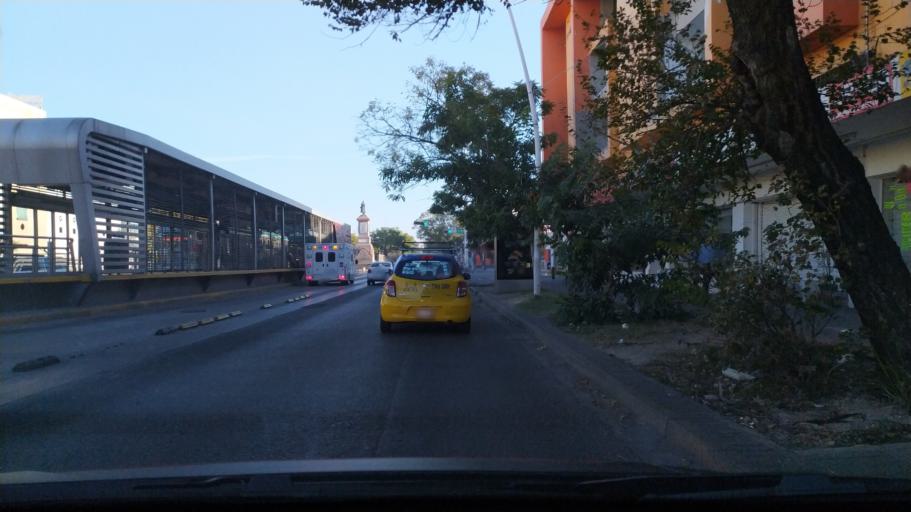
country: MX
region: Jalisco
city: Guadalajara
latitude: 20.6665
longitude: -103.3465
